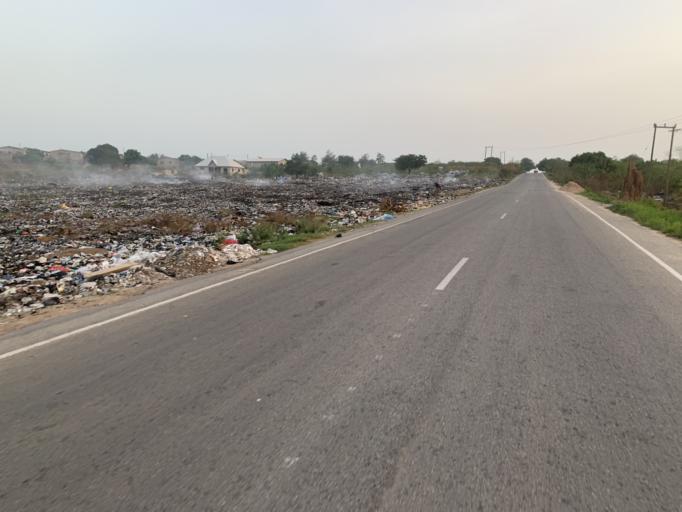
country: GH
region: Central
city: Winneba
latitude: 5.3627
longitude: -0.6091
